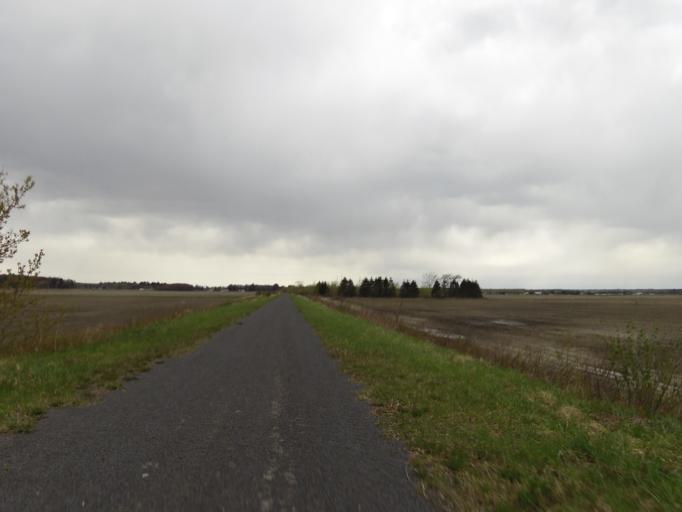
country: CA
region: Ontario
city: Bourget
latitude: 45.4466
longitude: -75.1257
